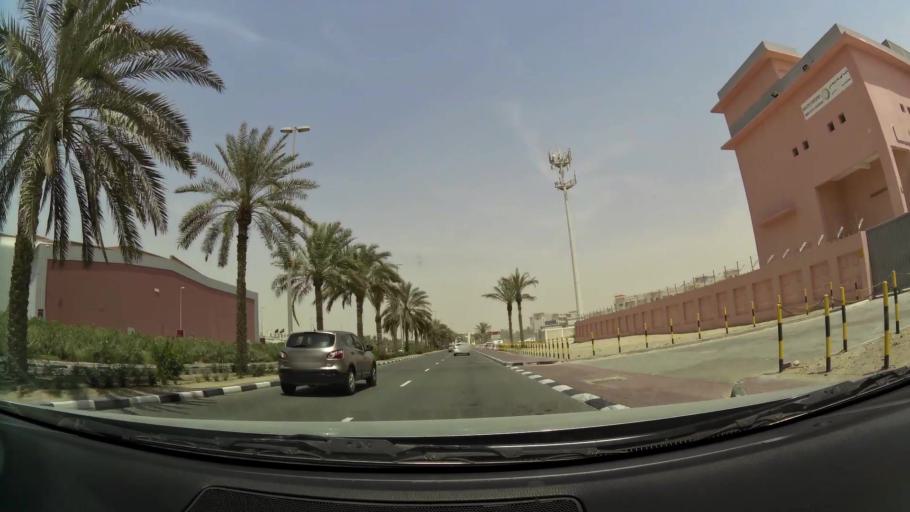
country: AE
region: Ash Shariqah
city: Sharjah
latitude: 25.1734
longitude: 55.4122
